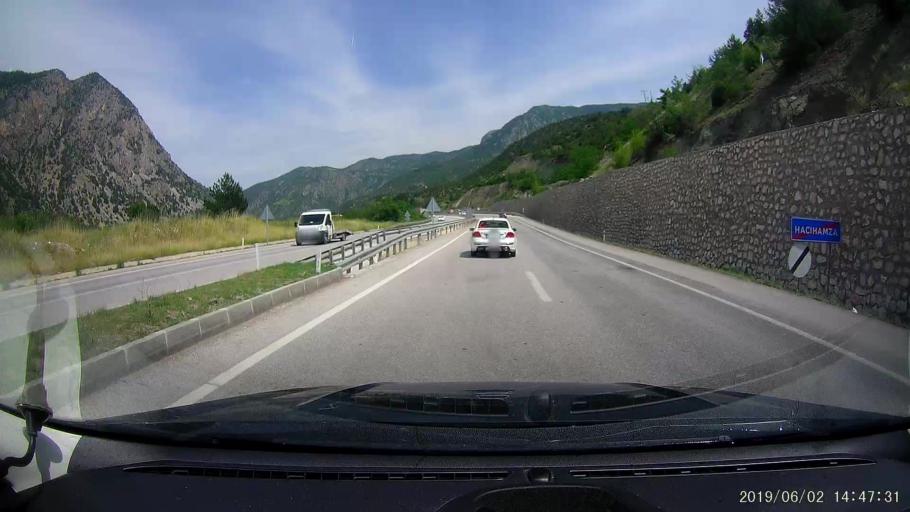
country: TR
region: Corum
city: Hacihamza
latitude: 41.0675
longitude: 34.4618
